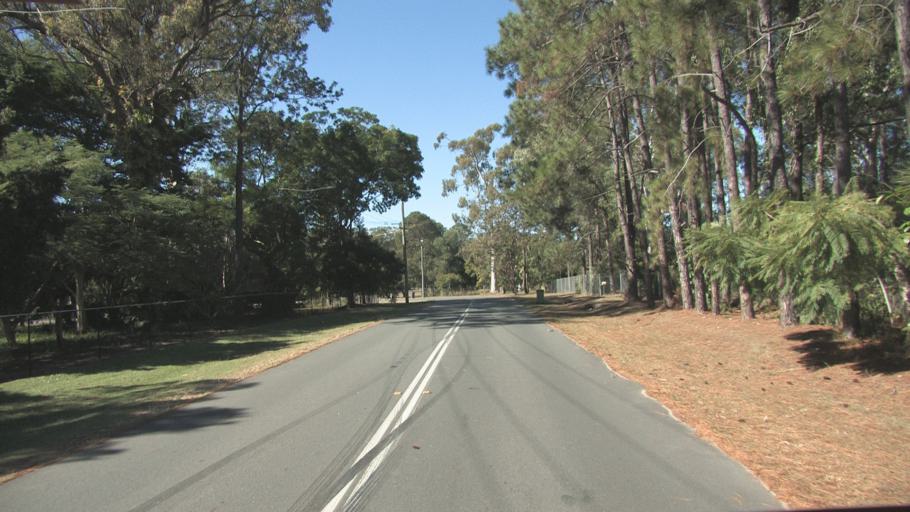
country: AU
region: Queensland
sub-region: Logan
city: Logan Reserve
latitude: -27.7044
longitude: 153.0609
